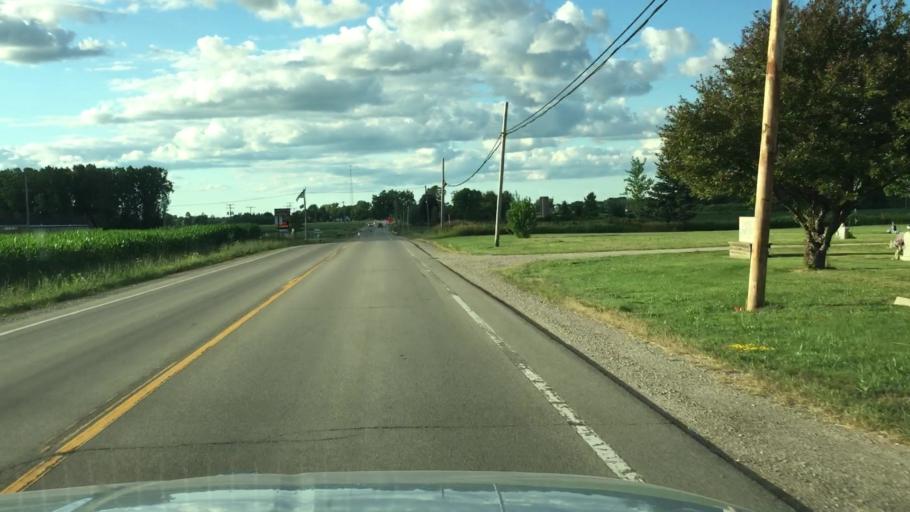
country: US
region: Michigan
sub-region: Saint Clair County
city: Capac
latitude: 42.9944
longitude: -82.9280
